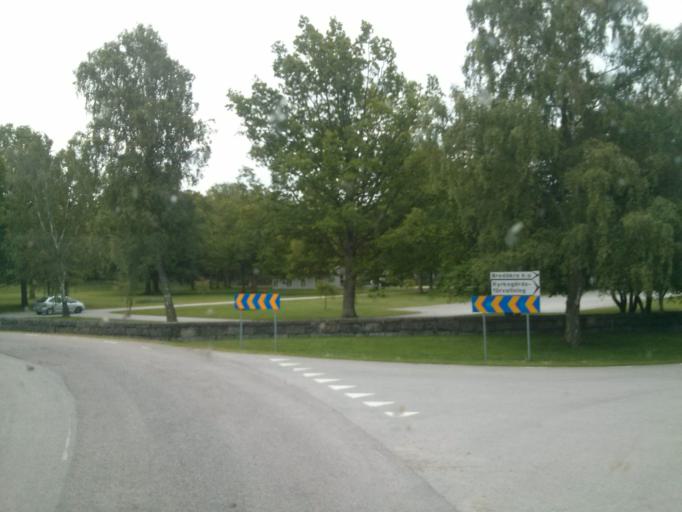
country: SE
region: Blekinge
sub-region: Ronneby Kommun
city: Kallinge
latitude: 56.2557
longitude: 15.2510
